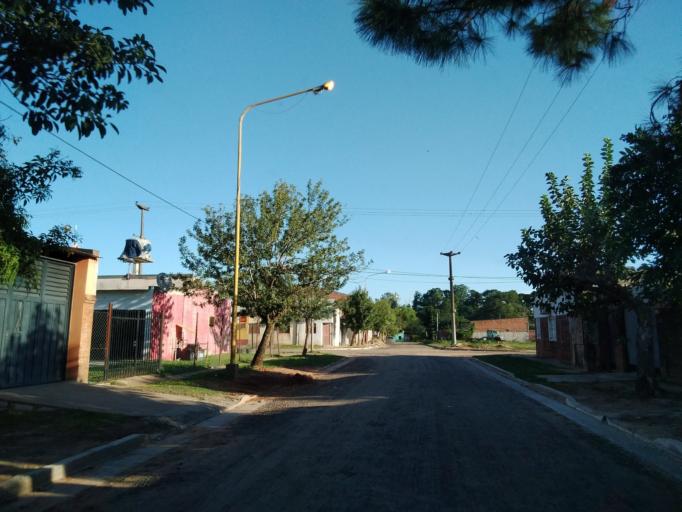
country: AR
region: Corrientes
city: Corrientes
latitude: -27.5053
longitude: -58.8024
